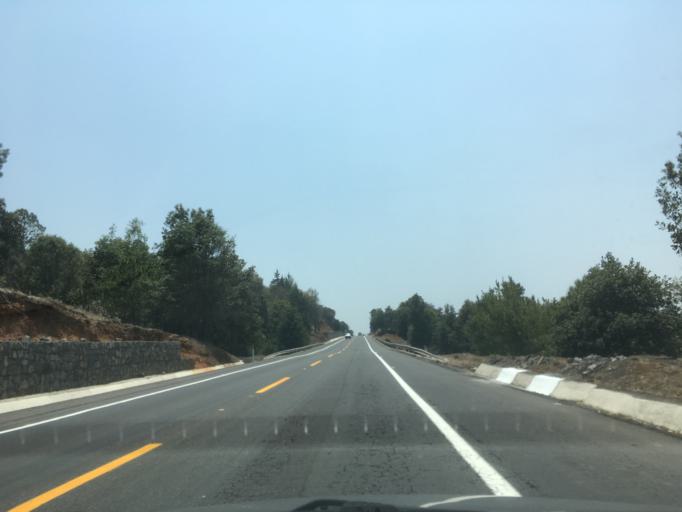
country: MX
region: Michoacan
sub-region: Patzcuaro
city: Santa Ana Chapitiro
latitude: 19.5064
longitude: -101.6762
